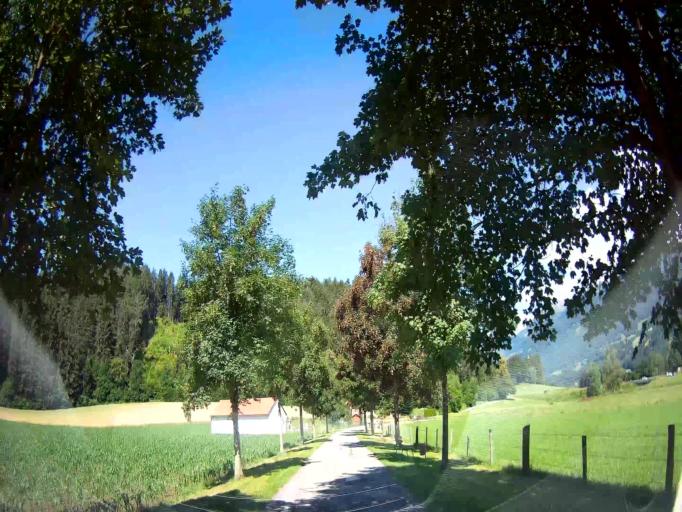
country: AT
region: Carinthia
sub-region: Politischer Bezirk Spittal an der Drau
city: Lendorf
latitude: 46.8230
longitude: 13.4455
